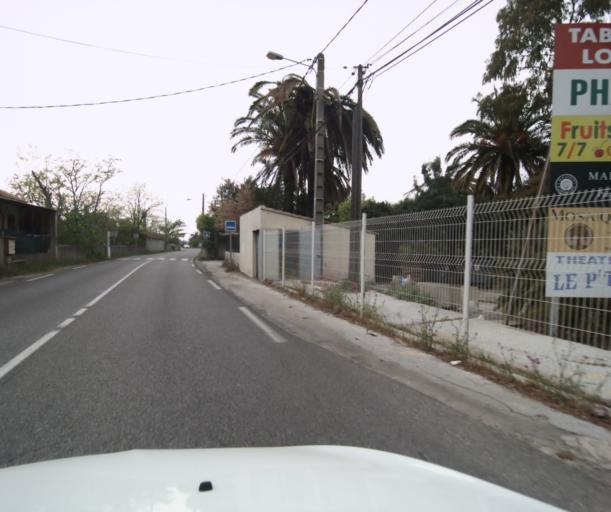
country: FR
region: Provence-Alpes-Cote d'Azur
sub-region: Departement du Var
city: La Garde
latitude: 43.1130
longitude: 5.9968
